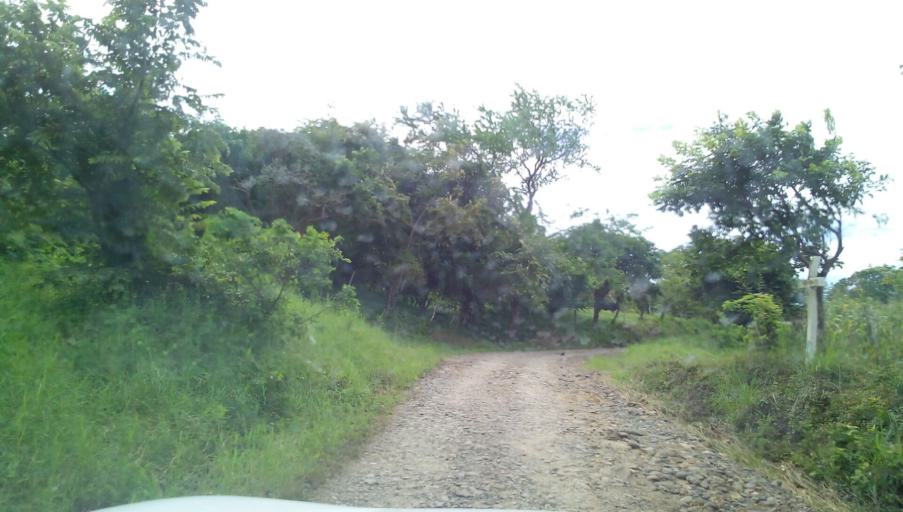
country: MX
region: Veracruz
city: Tepetzintla
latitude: 21.1329
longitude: -97.8508
